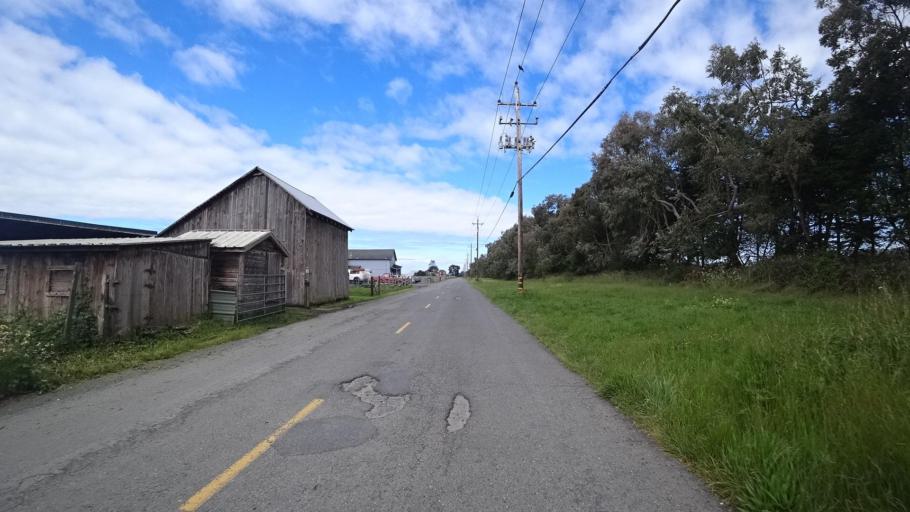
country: US
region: California
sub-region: Humboldt County
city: Arcata
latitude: 40.8814
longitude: -124.1015
